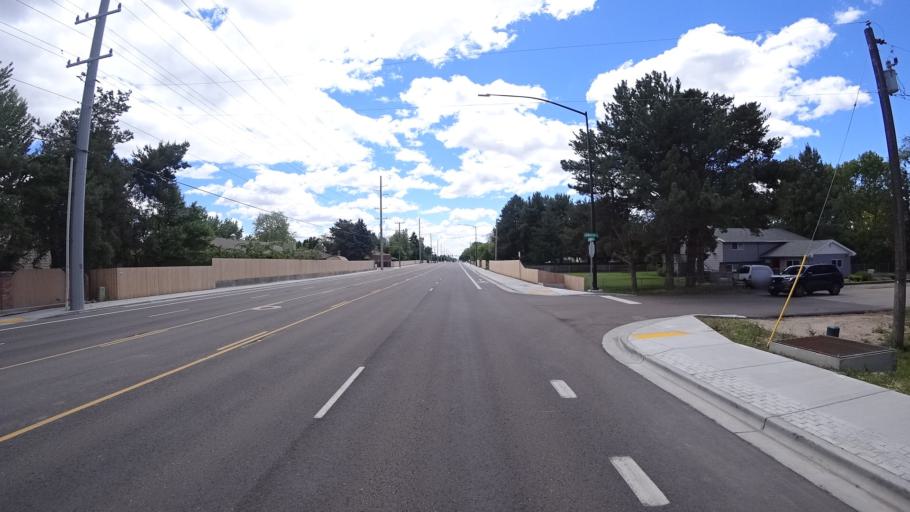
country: US
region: Idaho
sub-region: Ada County
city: Eagle
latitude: 43.6450
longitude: -116.3345
